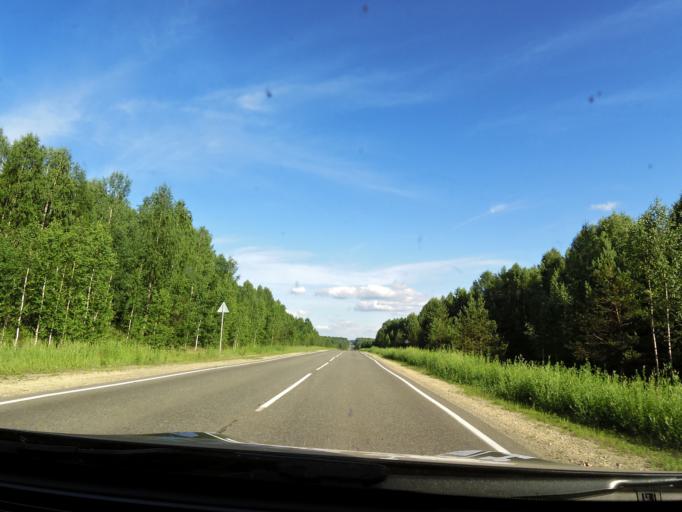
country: RU
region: Kirov
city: Chernaya Kholunitsa
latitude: 58.8109
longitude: 51.8350
